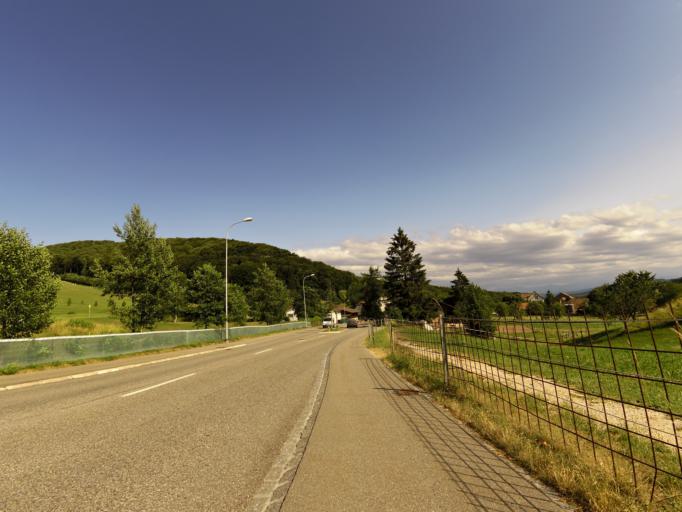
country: CH
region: Basel-Landschaft
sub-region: Bezirk Sissach
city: Laufelfingen
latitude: 47.3804
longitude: 7.8700
